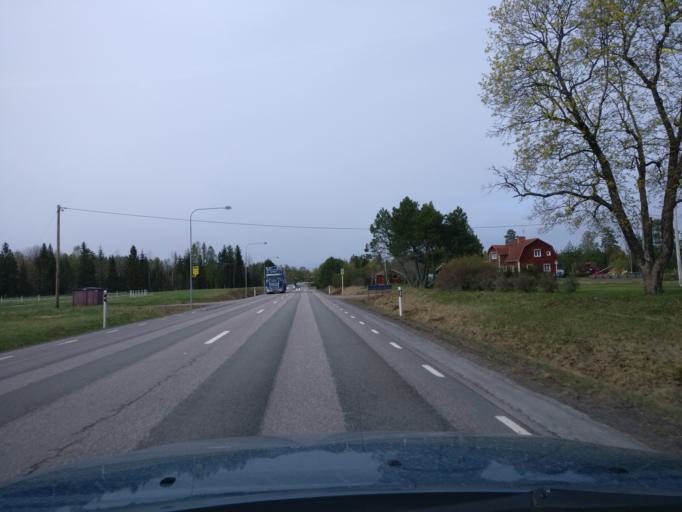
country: SE
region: Vaermland
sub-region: Munkfors Kommun
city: Munkfors
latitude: 59.8031
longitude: 13.5046
